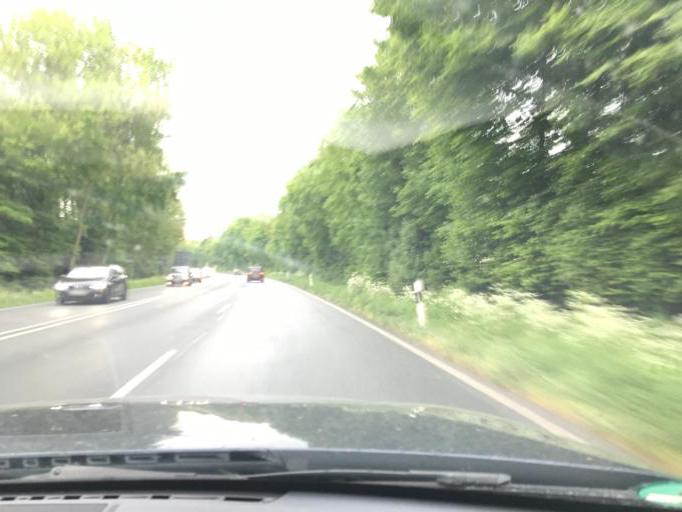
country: DE
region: North Rhine-Westphalia
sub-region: Regierungsbezirk Munster
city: Greven
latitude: 52.1068
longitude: 7.6252
